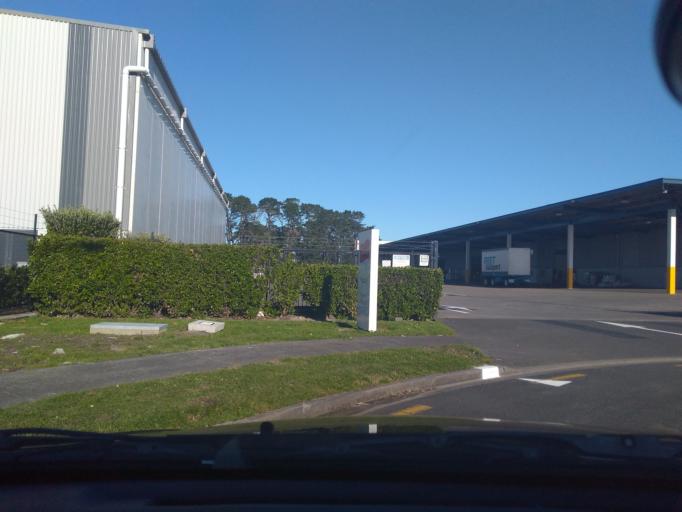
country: NZ
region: Auckland
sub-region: Auckland
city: Tamaki
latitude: -36.9288
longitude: 174.8763
